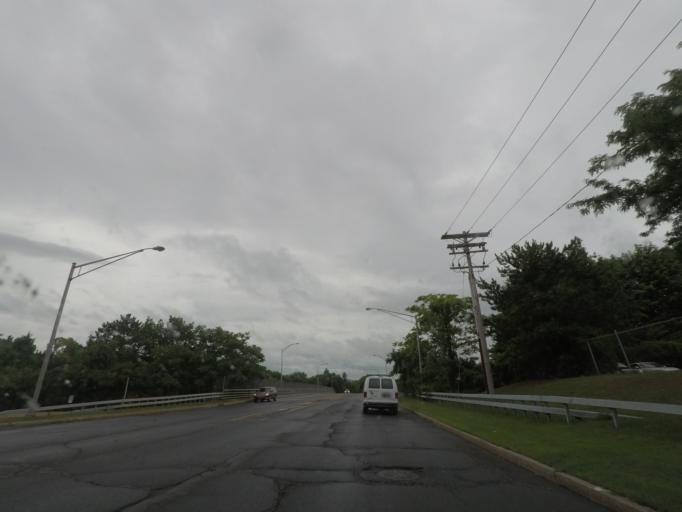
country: US
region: New York
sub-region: Albany County
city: Albany
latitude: 42.6724
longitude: -73.7482
